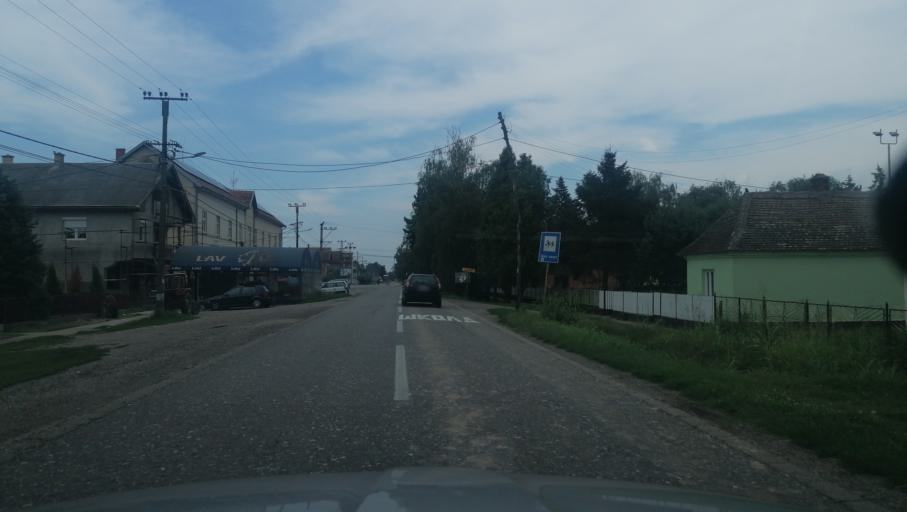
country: RS
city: Klenje
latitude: 44.8071
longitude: 19.4325
